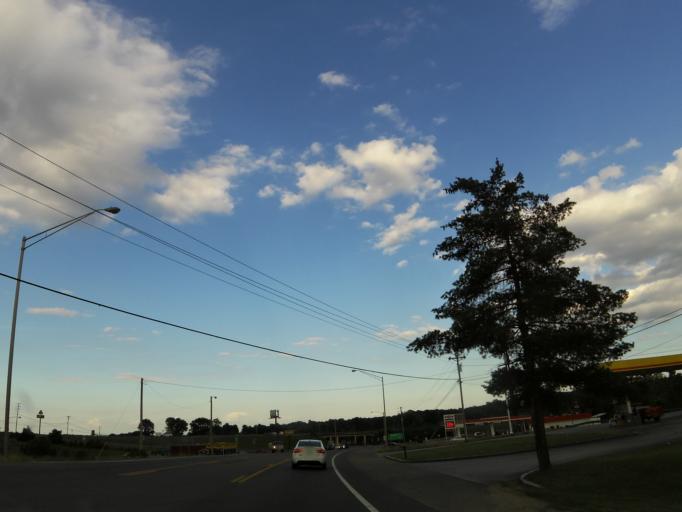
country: US
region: Tennessee
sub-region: Maury County
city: Spring Hill
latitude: 35.6432
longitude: -86.8970
